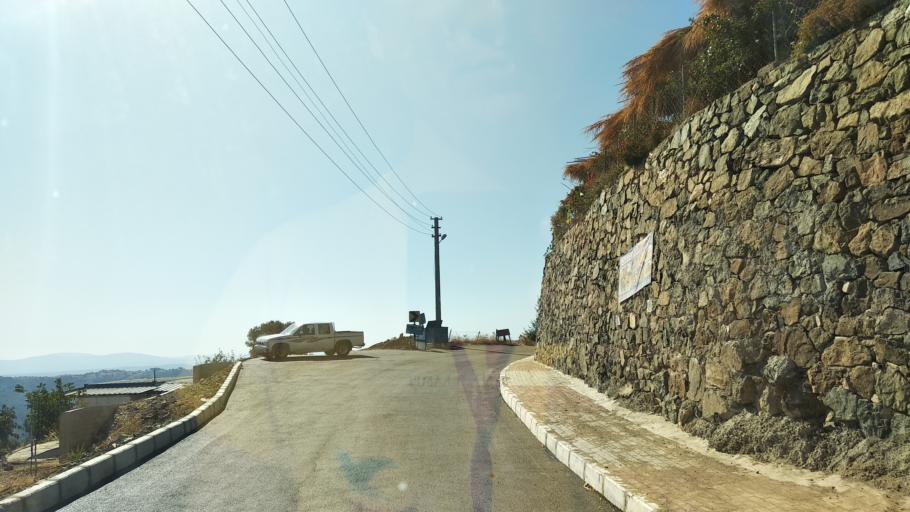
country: TR
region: Izmir
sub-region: Seferihisar
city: Seferhisar
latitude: 38.3120
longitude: 26.9554
